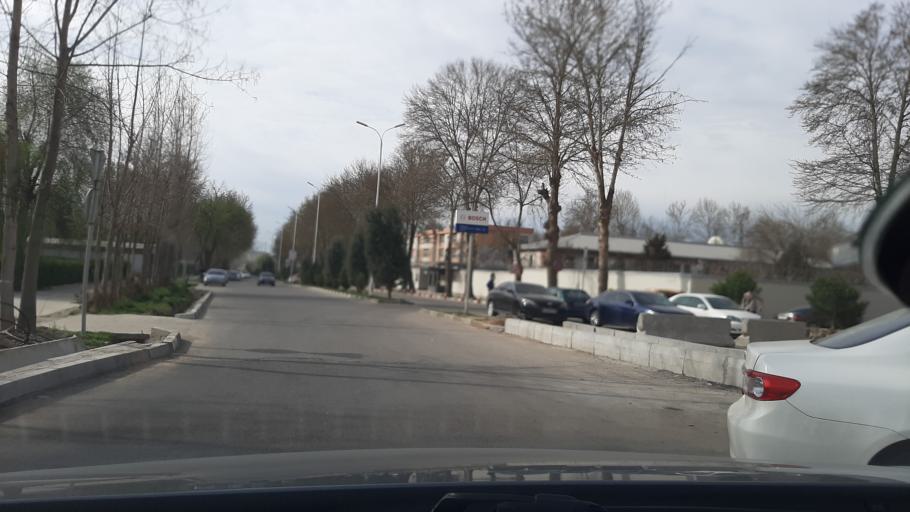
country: TJ
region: Dushanbe
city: Dushanbe
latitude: 38.5816
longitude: 68.7492
